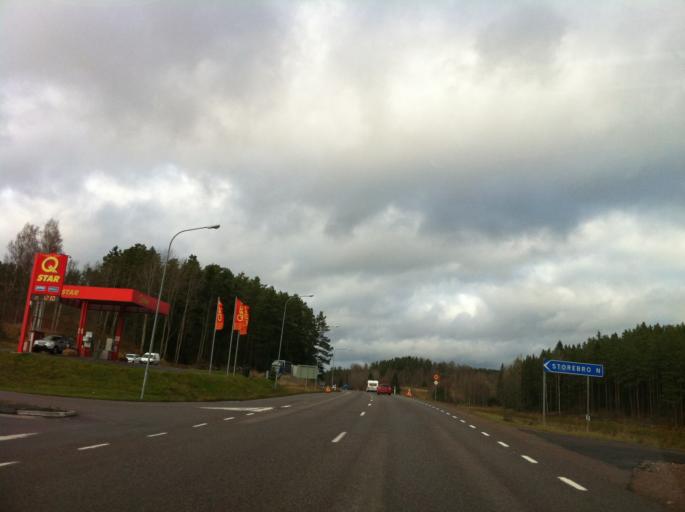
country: SE
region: Kalmar
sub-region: Vimmerby Kommun
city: Vimmerby
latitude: 57.5923
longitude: 15.8482
